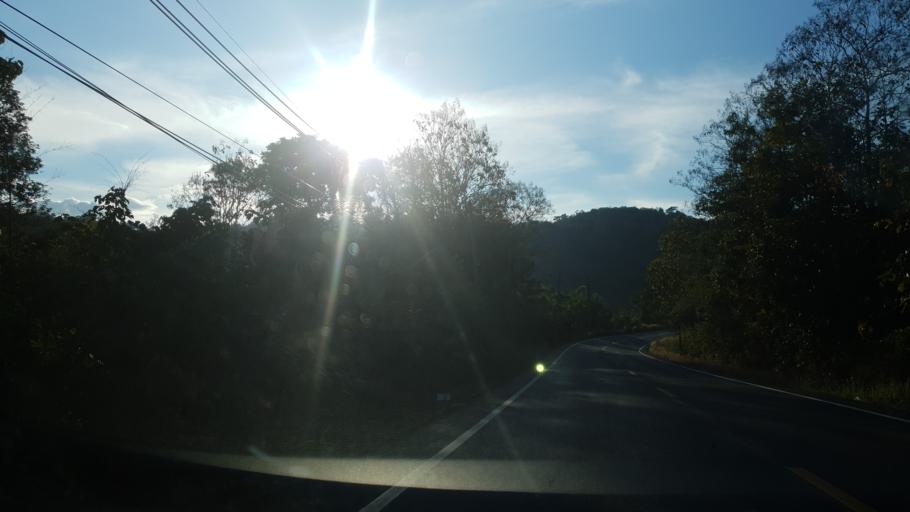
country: TH
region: Loei
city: Dan Sai
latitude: 17.2242
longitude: 101.0684
